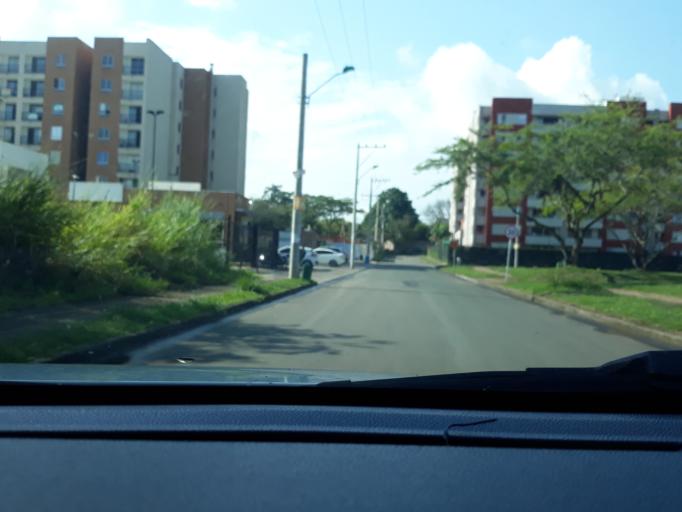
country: CO
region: Valle del Cauca
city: Cali
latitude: 3.3559
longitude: -76.5174
